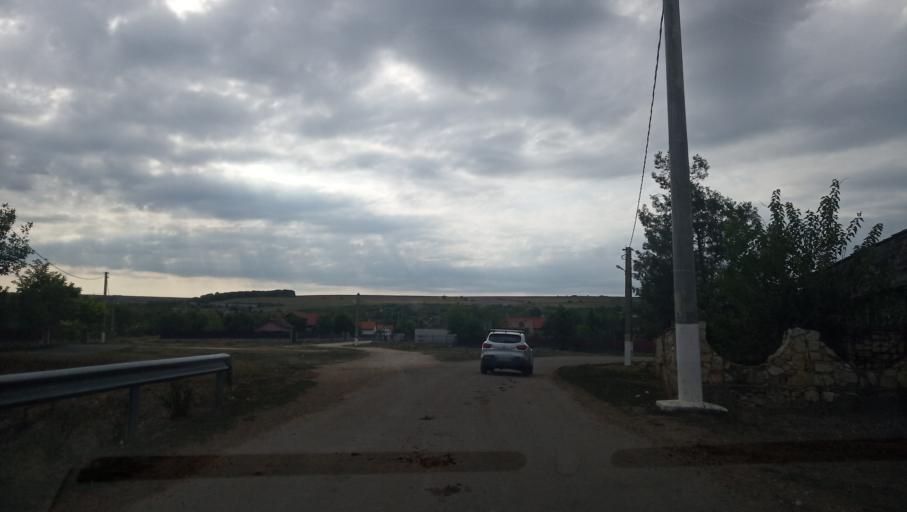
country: RO
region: Constanta
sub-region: Comuna Adamclisi
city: Adamclisi
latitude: 44.0422
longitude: 27.9624
